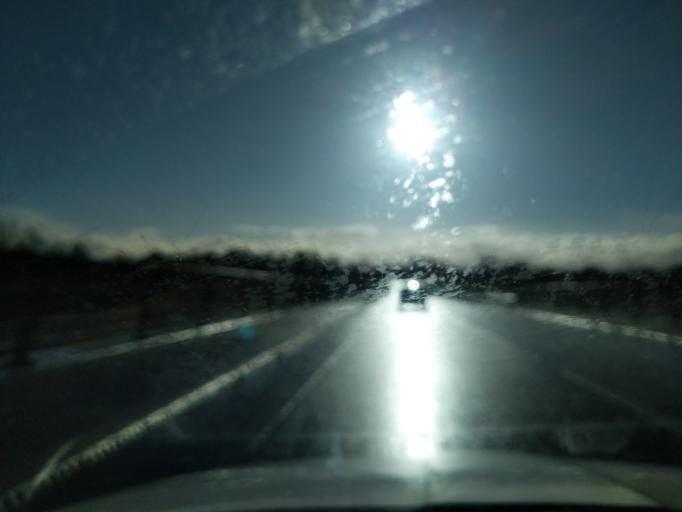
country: GB
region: England
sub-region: North Yorkshire
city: Bedale
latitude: 54.2952
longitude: -1.5931
